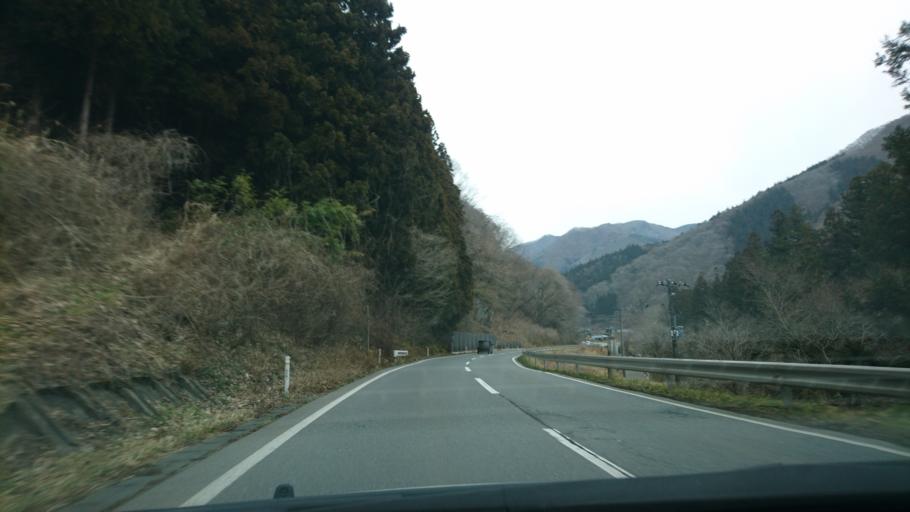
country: JP
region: Iwate
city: Tono
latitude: 39.2078
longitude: 141.5920
